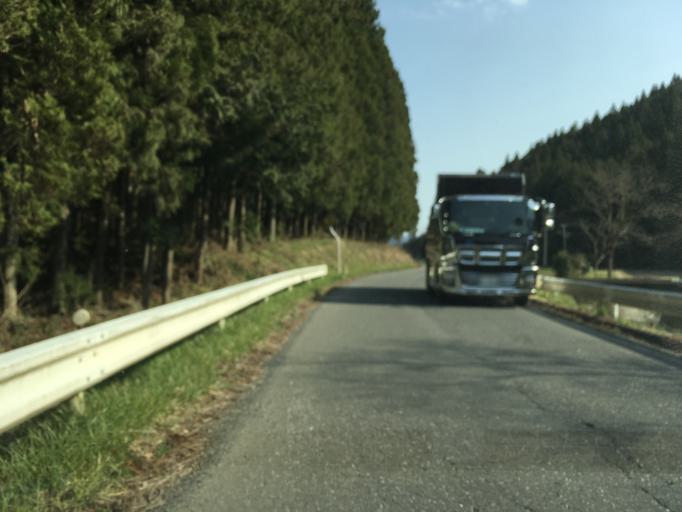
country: JP
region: Iwate
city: Ichinoseki
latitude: 38.8057
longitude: 141.3159
